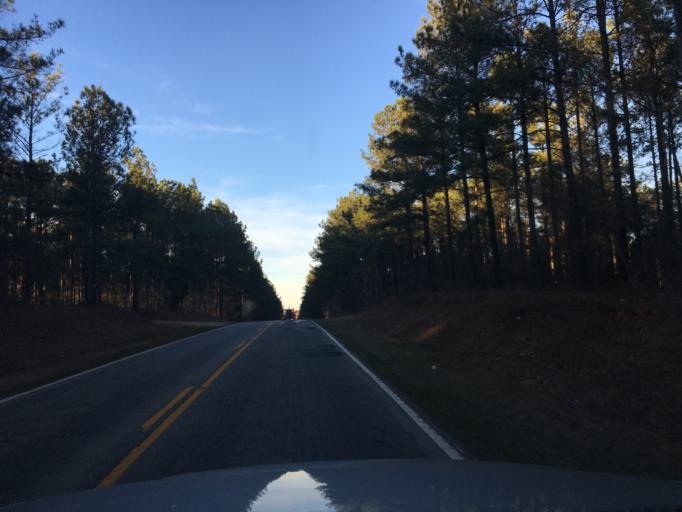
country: US
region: South Carolina
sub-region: Greenwood County
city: Ninety Six
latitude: 34.2176
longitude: -81.8803
